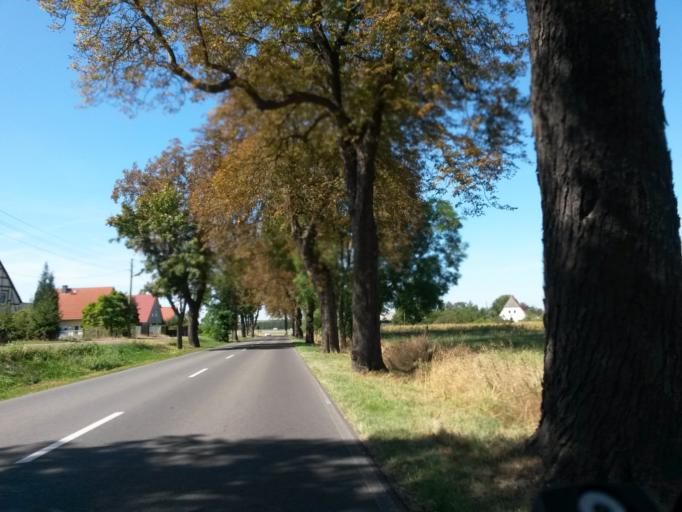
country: DE
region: Saxony-Anhalt
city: Arneburg
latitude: 52.6723
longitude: 11.9766
